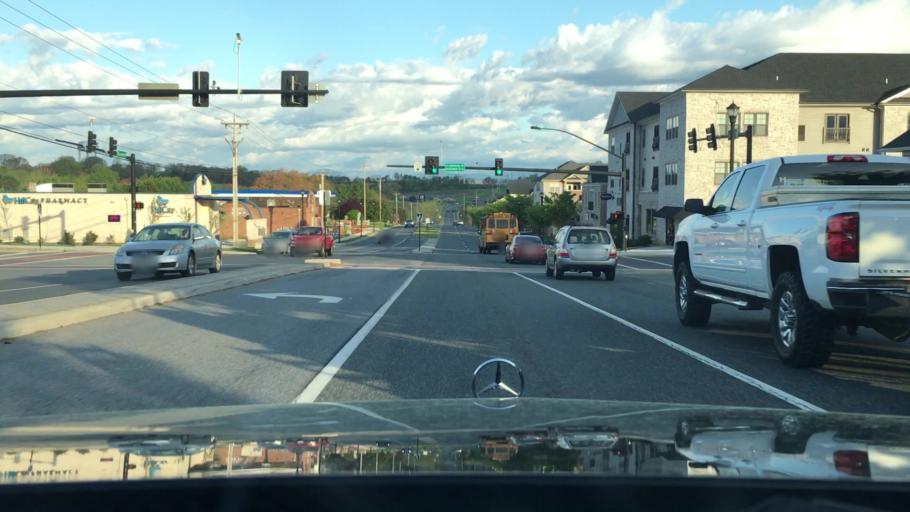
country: US
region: Virginia
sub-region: Campbell County
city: Timberlake
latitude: 37.3392
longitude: -79.2249
